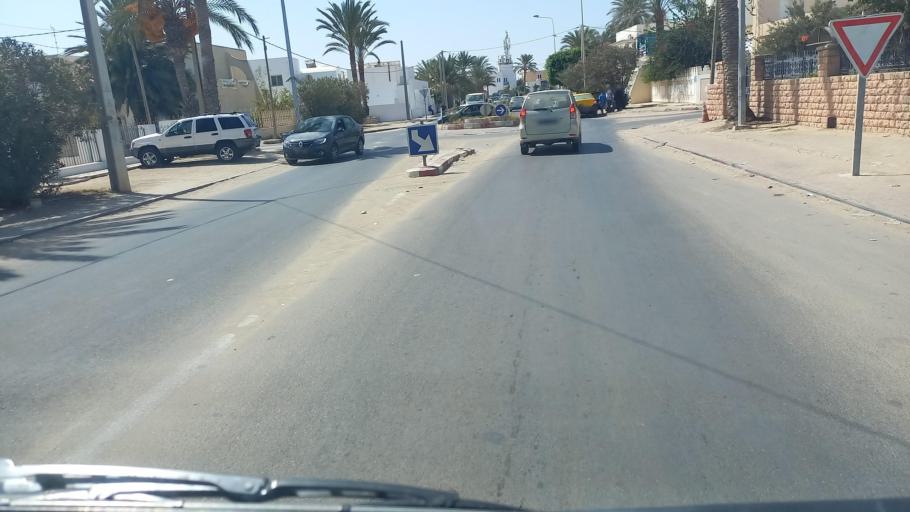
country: TN
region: Madanin
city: Houmt Souk
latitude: 33.8742
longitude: 10.8741
